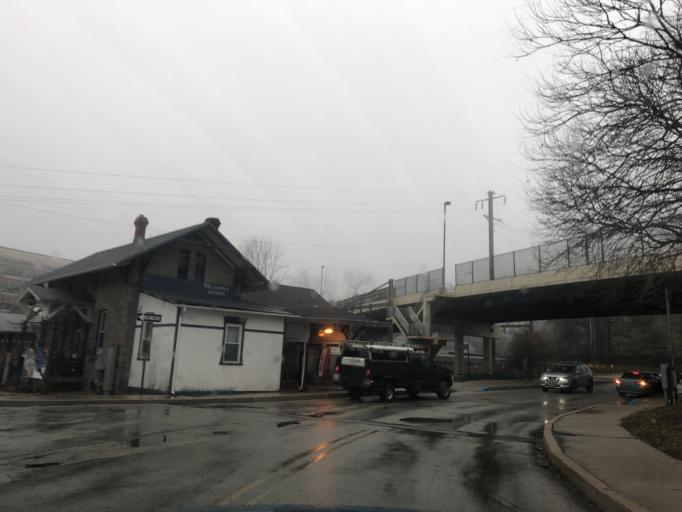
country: US
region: Pennsylvania
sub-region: Delaware County
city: Radnor
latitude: 40.0389
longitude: -75.3418
